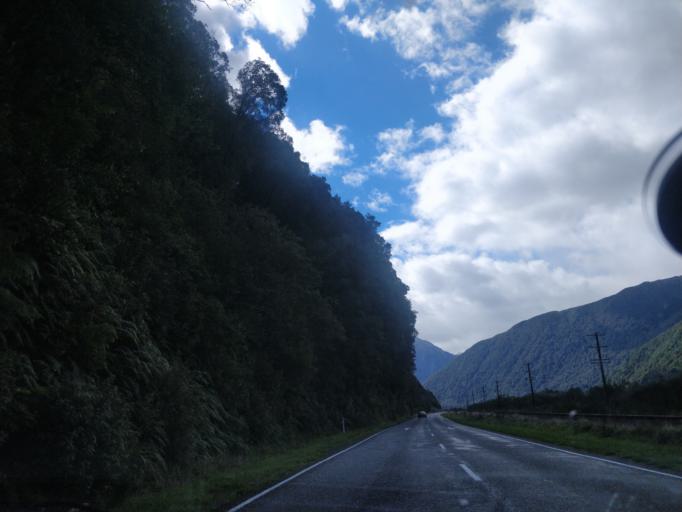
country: NZ
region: West Coast
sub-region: Grey District
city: Greymouth
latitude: -42.7925
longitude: 171.5936
